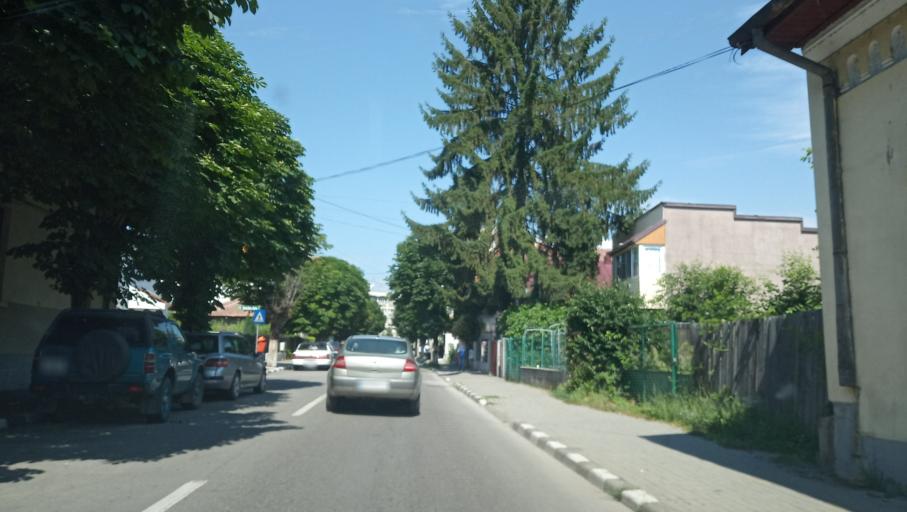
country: RO
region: Valcea
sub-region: Municipiul Ramnicu Valcea
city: Ramnicu Valcea
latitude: 45.0954
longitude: 24.3638
